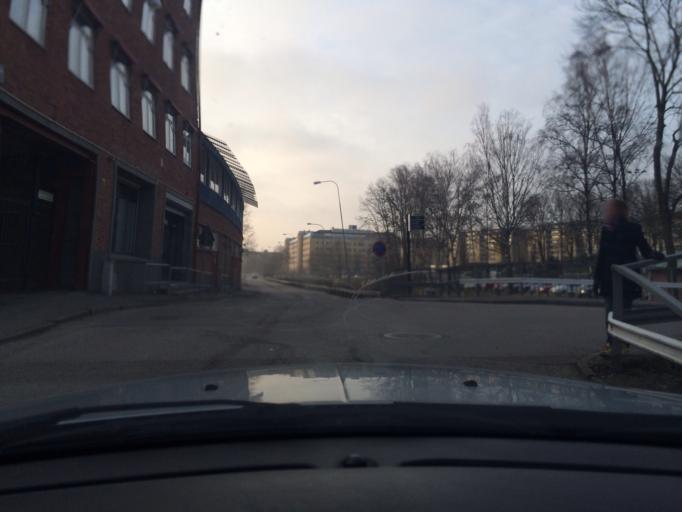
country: SE
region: Vaestra Goetaland
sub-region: Goteborg
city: Goeteborg
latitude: 57.6924
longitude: 11.9950
